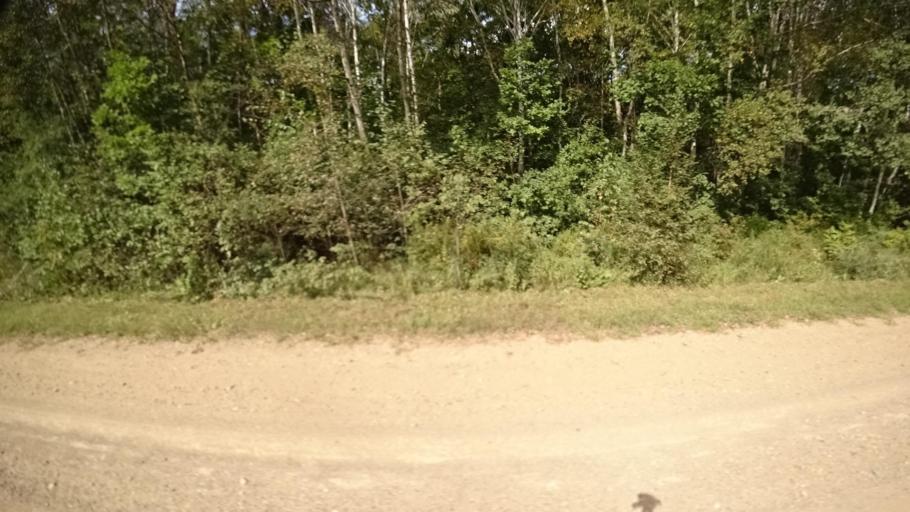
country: RU
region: Primorskiy
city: Yakovlevka
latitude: 44.7038
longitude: 133.6392
